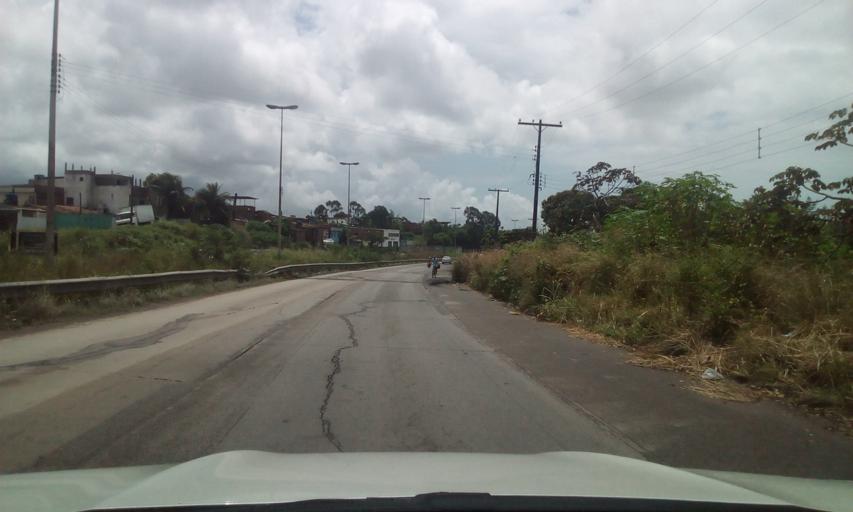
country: BR
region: Pernambuco
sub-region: Jaboatao Dos Guararapes
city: Jaboatao dos Guararapes
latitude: -8.0877
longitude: -34.9466
